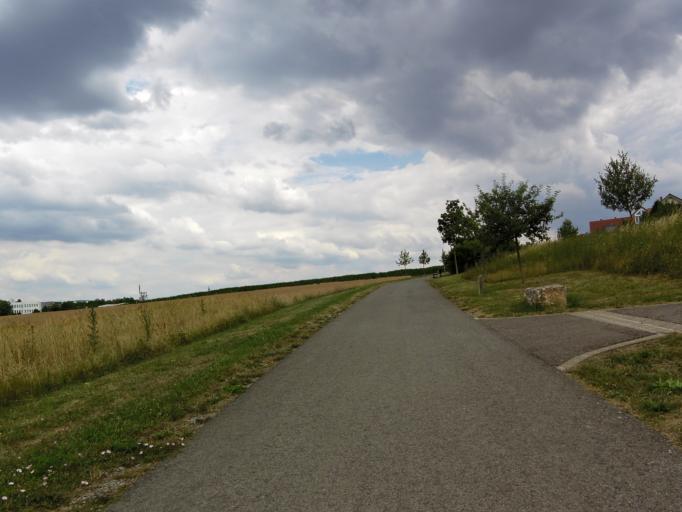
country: DE
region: Bavaria
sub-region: Regierungsbezirk Unterfranken
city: Eibelstadt
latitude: 49.7256
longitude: 9.9628
